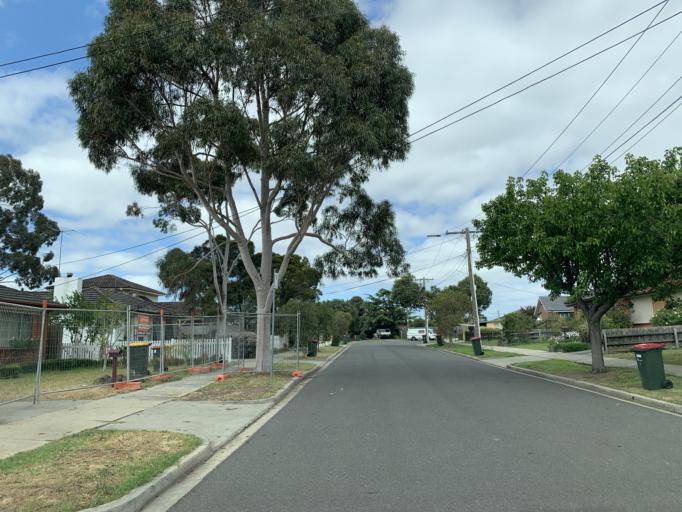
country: AU
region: Victoria
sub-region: Moonee Valley
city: Keilor East
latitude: -37.7442
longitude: 144.8612
